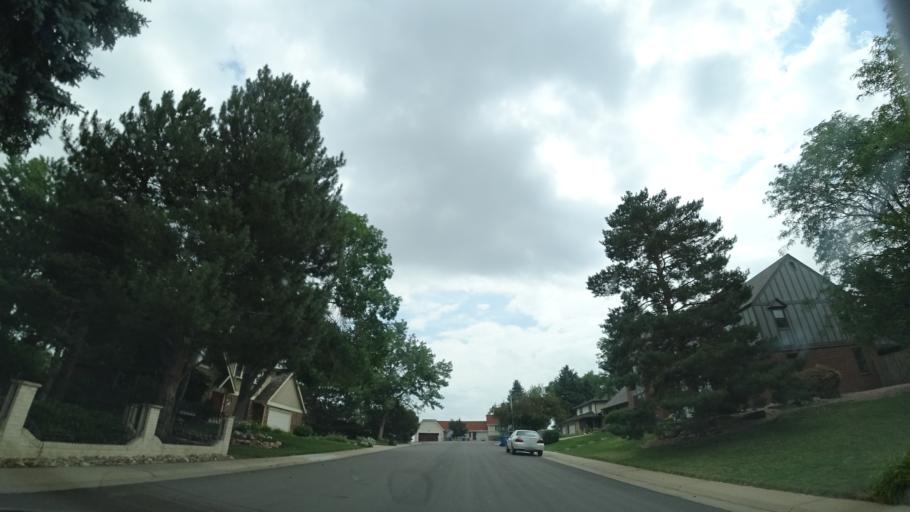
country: US
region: Colorado
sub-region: Jefferson County
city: West Pleasant View
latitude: 39.7129
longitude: -105.1557
